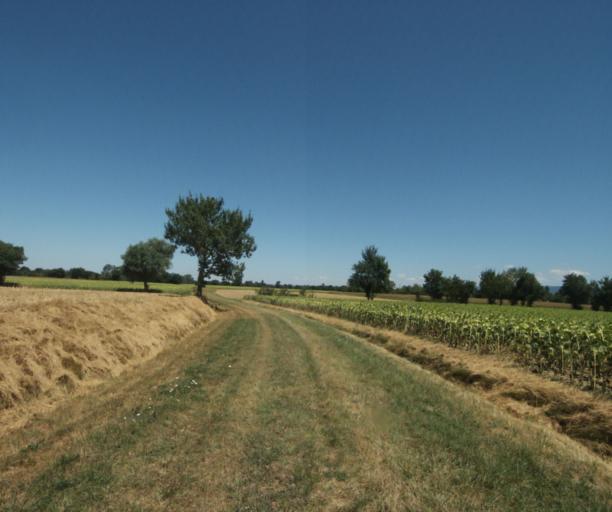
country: FR
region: Midi-Pyrenees
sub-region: Departement de la Haute-Garonne
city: Revel
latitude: 43.4759
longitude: 1.9453
